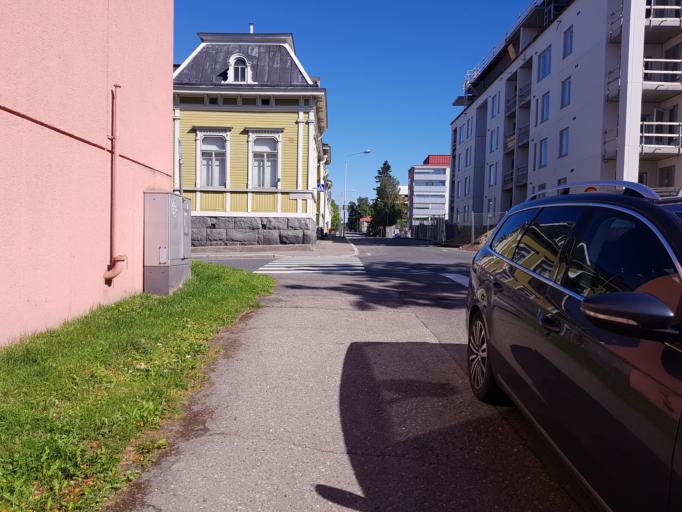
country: FI
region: Northern Savo
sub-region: Kuopio
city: Kuopio
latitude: 62.8881
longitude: 27.6861
